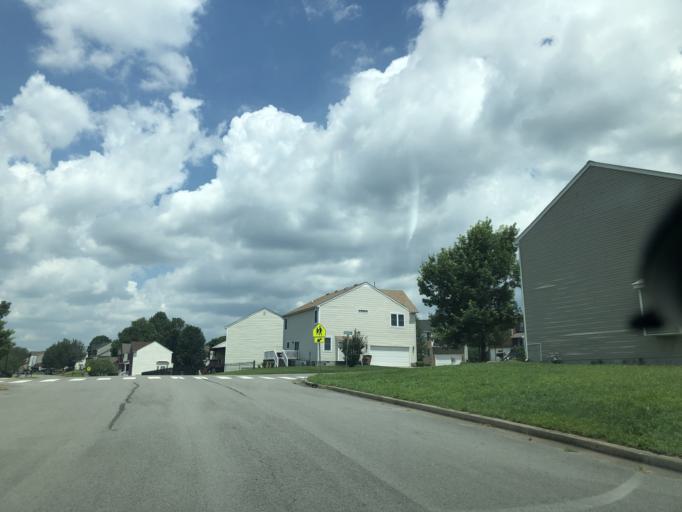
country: US
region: Tennessee
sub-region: Rutherford County
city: La Vergne
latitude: 36.0412
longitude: -86.6204
